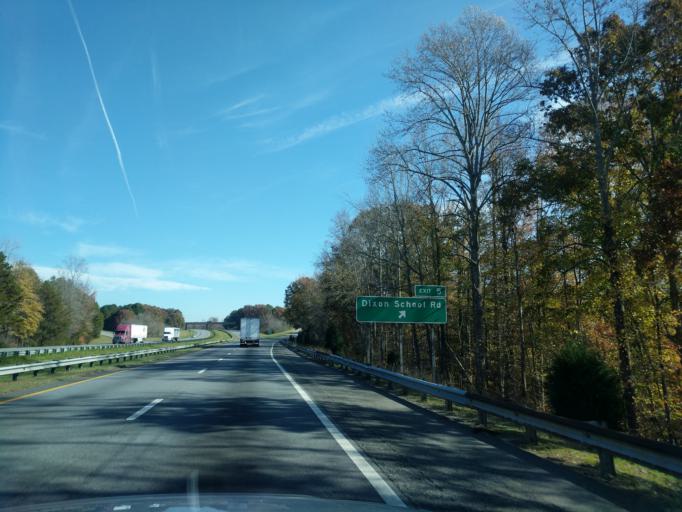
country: US
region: North Carolina
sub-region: Cleveland County
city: White Plains
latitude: 35.1983
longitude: -81.3760
